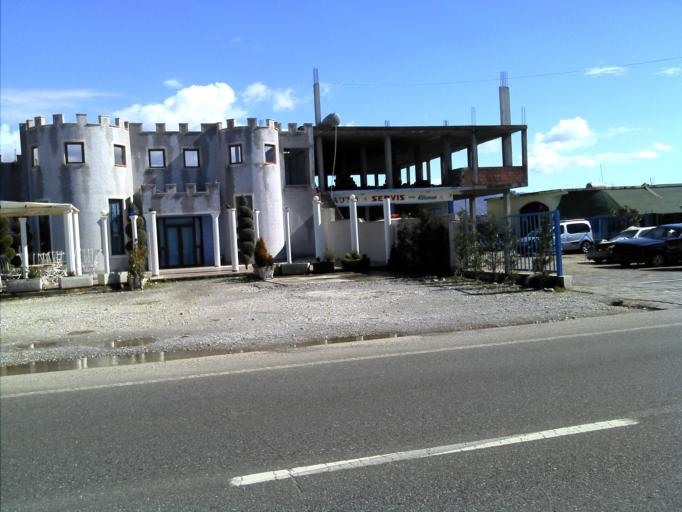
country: AL
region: Shkoder
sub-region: Rrethi i Malesia e Madhe
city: Grude-Fushe
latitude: 42.1627
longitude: 19.4699
